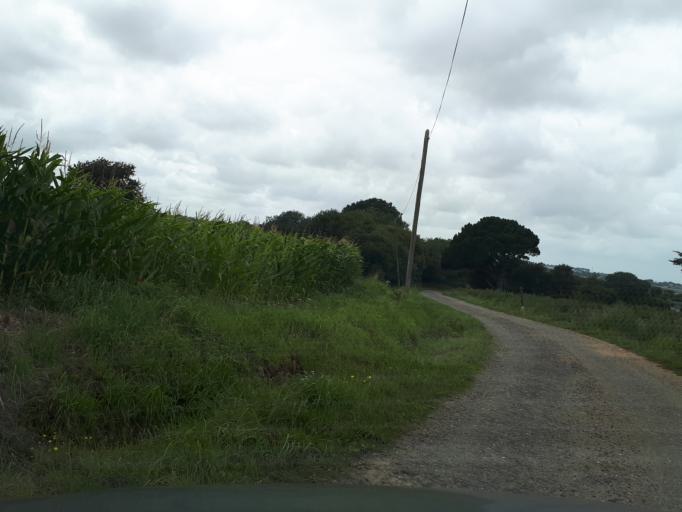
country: FR
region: Brittany
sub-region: Departement du Finistere
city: Carantec
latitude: 48.6542
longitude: -3.9225
